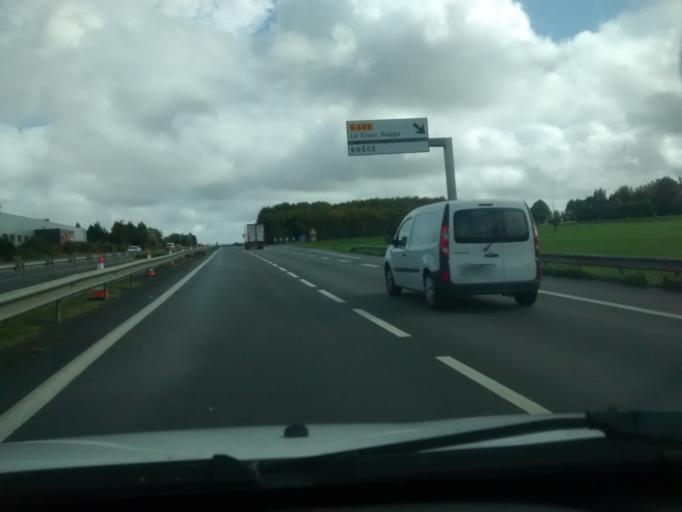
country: FR
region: Brittany
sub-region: Departement d'Ille-et-Vilaine
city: Brece
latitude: 48.1035
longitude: -1.4906
